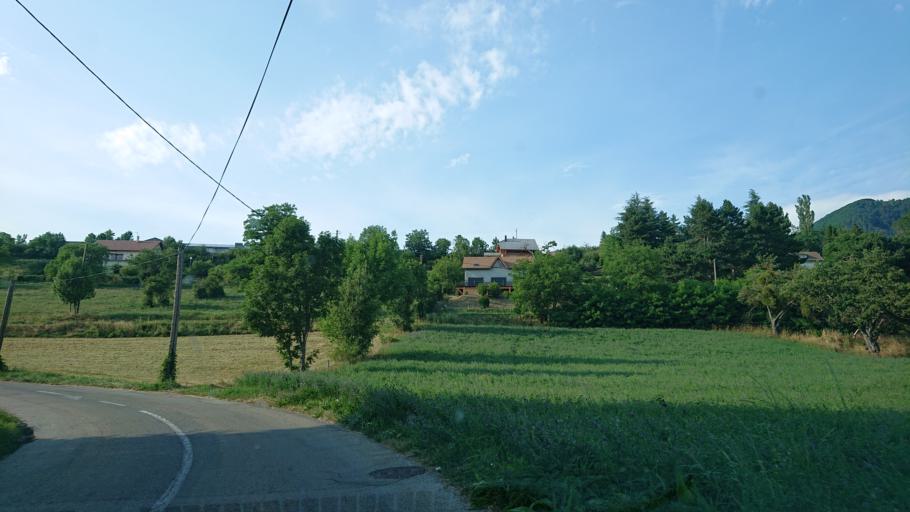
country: FR
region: Rhone-Alpes
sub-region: Departement de l'Isere
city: La Mure
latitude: 44.8189
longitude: 5.9332
